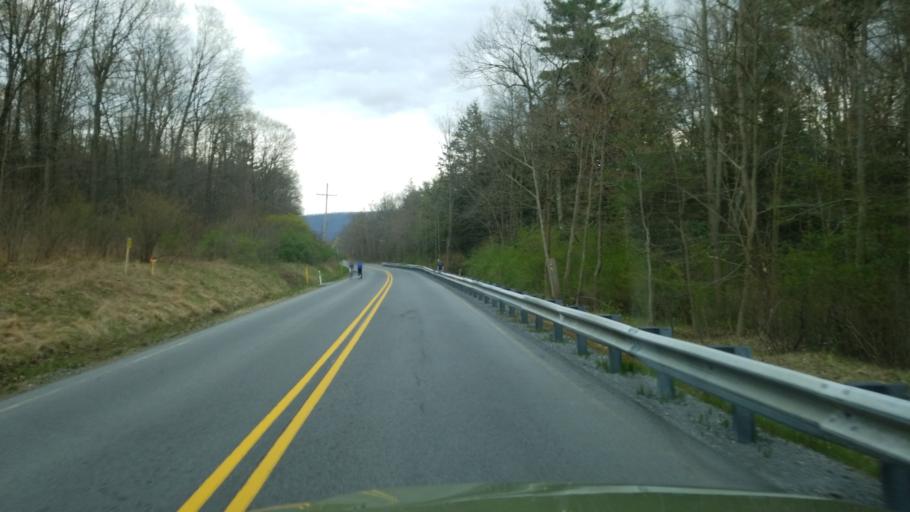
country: US
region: Pennsylvania
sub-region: Blair County
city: Tipton
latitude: 40.6515
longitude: -78.3246
